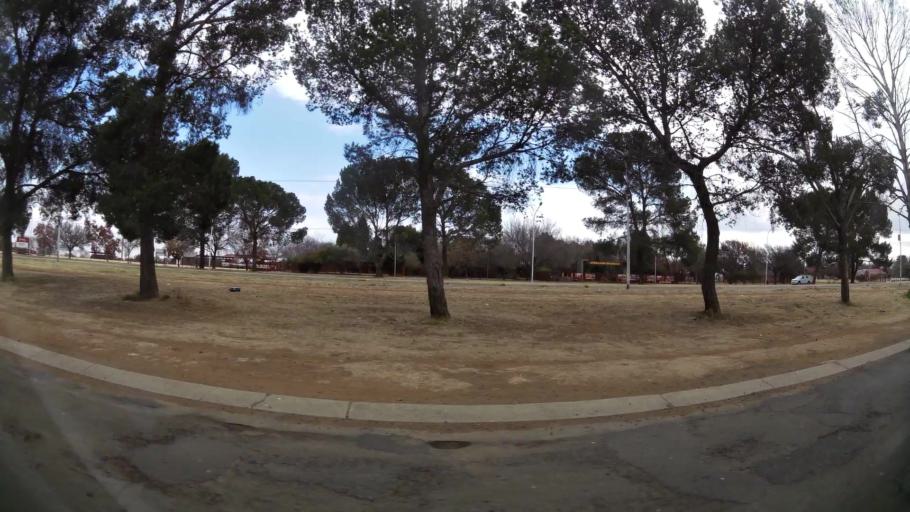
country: ZA
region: Orange Free State
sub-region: Fezile Dabi District Municipality
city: Kroonstad
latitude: -27.6372
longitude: 27.2339
